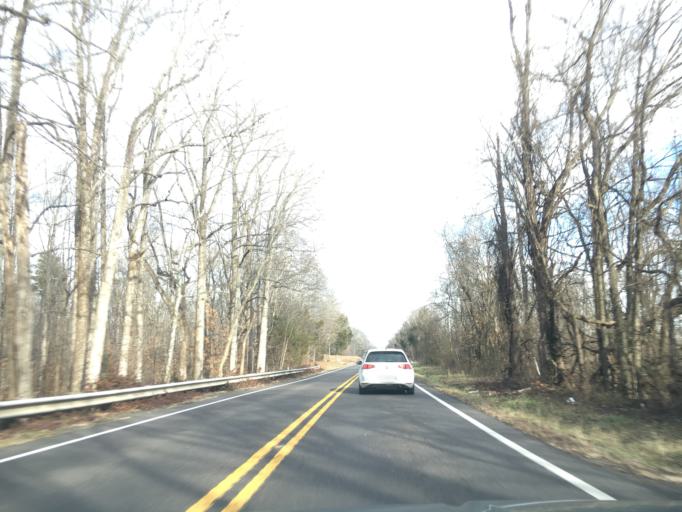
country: US
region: Virginia
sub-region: Culpeper County
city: Culpeper
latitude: 38.5832
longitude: -77.9757
